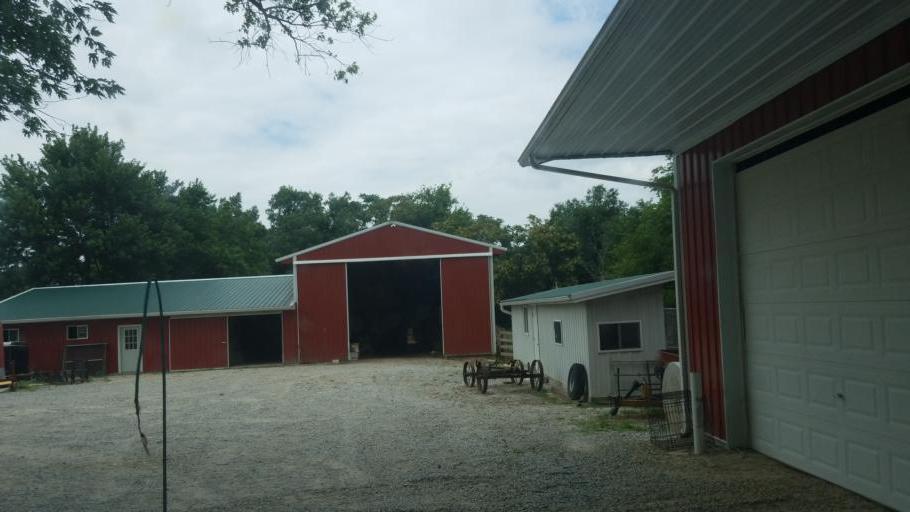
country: US
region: Illinois
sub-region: Jackson County
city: Murphysboro
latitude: 37.7061
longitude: -89.3474
